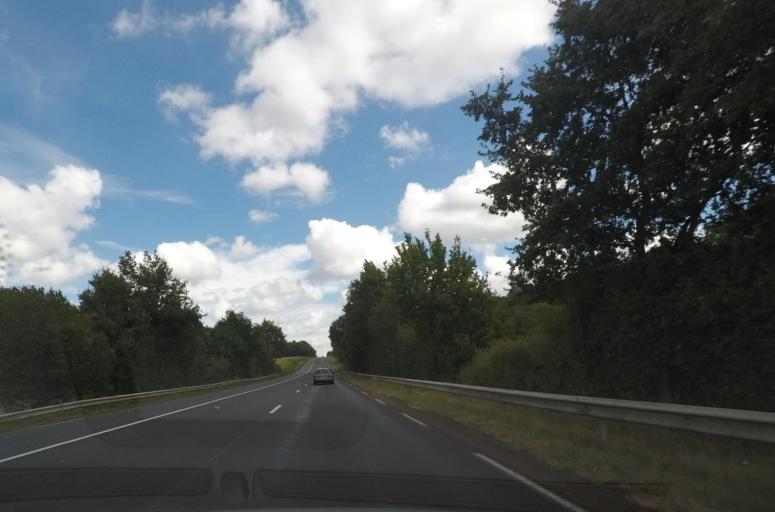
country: FR
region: Pays de la Loire
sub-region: Departement de la Sarthe
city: Clermont-Creans
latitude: 47.7517
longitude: 0.0062
